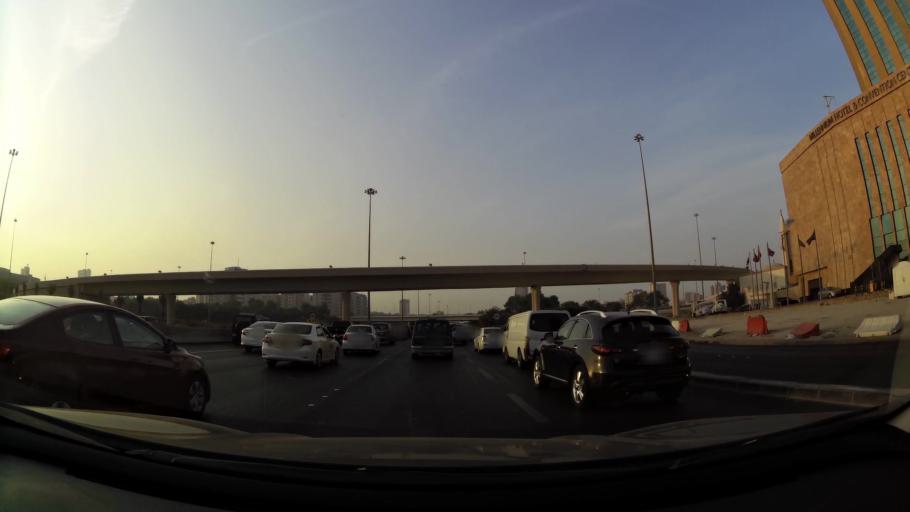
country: KW
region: Muhafazat Hawalli
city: Hawalli
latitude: 29.3292
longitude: 48.0411
